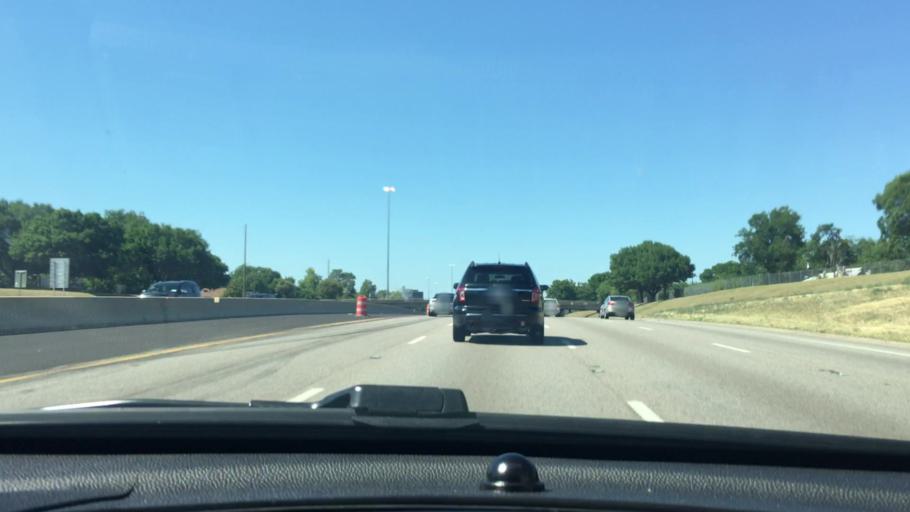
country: US
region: Texas
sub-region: Dallas County
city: Cockrell Hill
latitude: 32.7212
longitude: -96.8272
